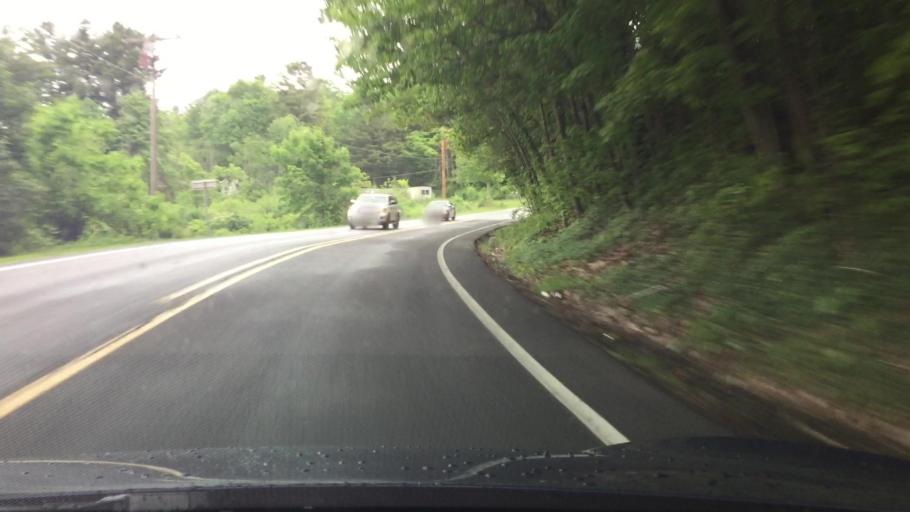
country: US
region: West Virginia
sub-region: Raleigh County
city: Shady Spring
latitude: 37.6931
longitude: -81.0678
